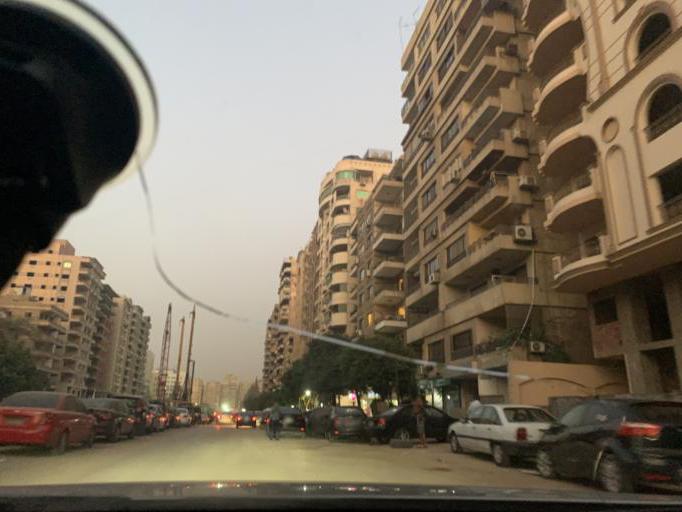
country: EG
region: Muhafazat al Qahirah
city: Cairo
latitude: 30.0625
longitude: 31.3419
